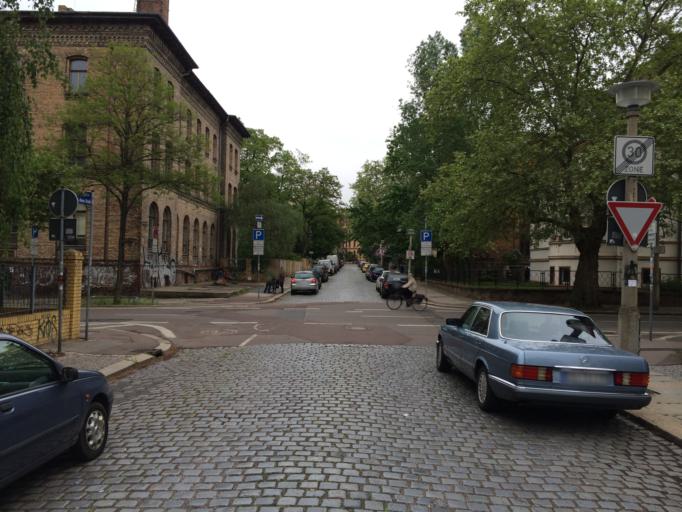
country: DE
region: Saxony-Anhalt
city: Halle (Saale)
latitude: 51.4902
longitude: 11.9693
